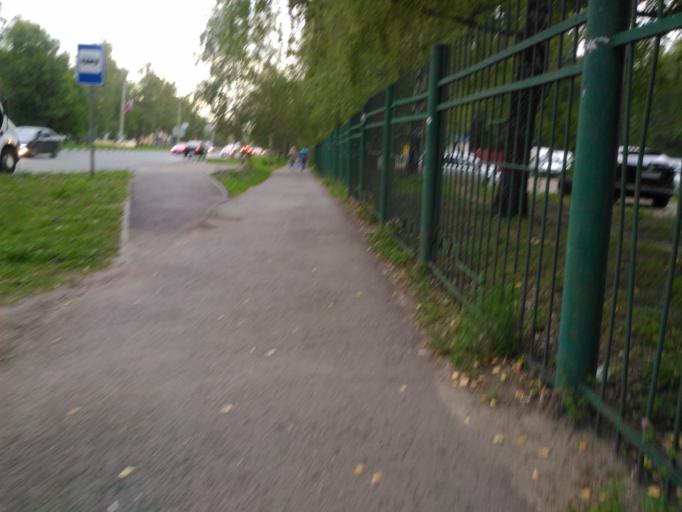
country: RU
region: Ulyanovsk
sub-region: Ulyanovskiy Rayon
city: Ulyanovsk
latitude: 54.2637
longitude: 48.3349
